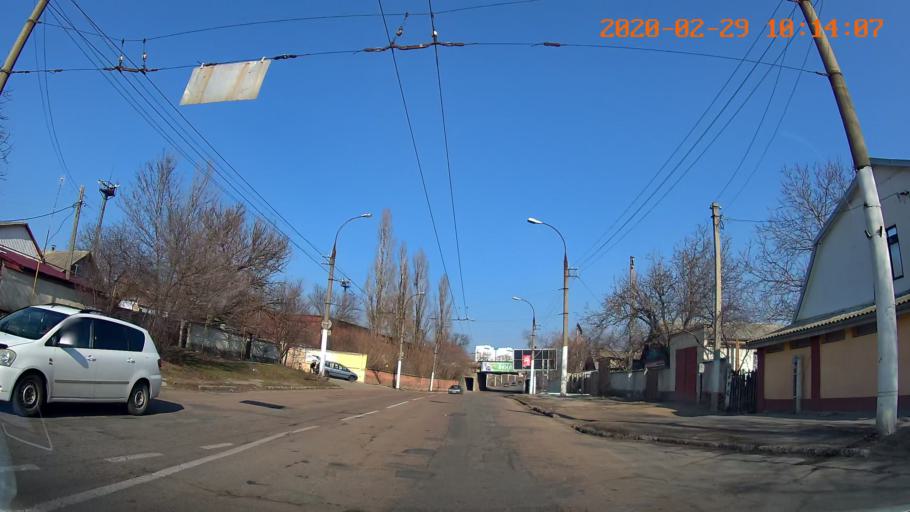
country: MD
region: Telenesti
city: Tiraspolul Nou
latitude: 46.8440
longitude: 29.6444
